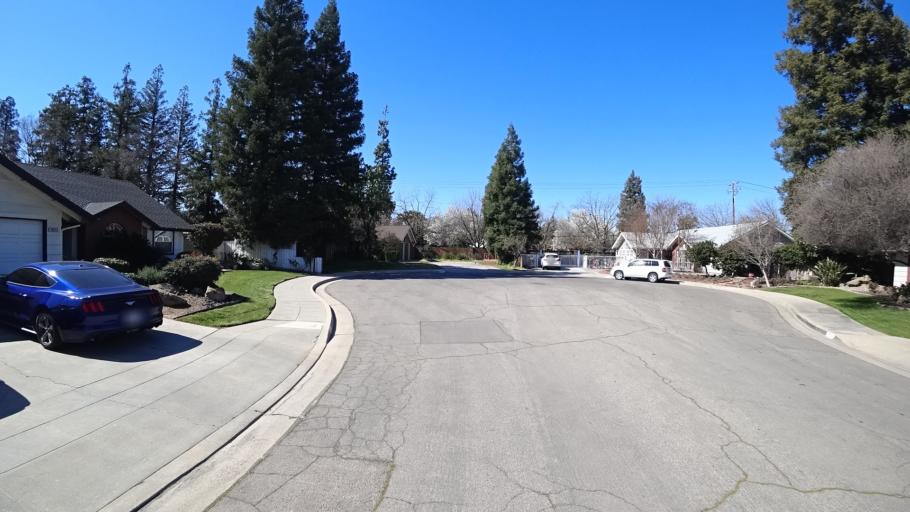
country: US
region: California
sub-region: Fresno County
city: Clovis
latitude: 36.8478
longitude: -119.7650
